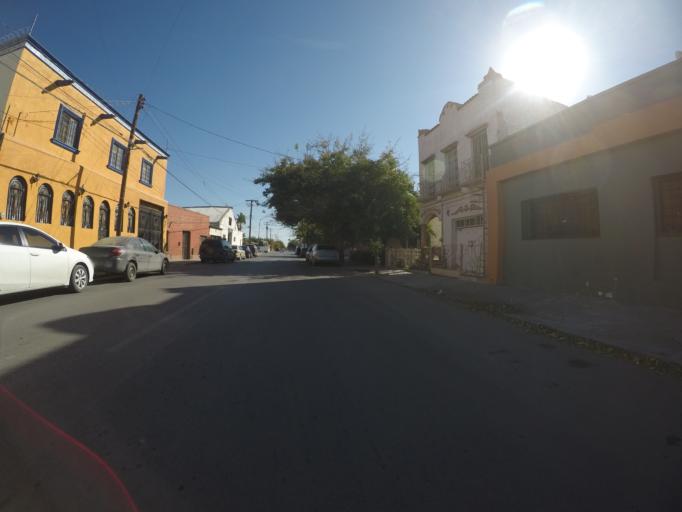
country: MX
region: Chihuahua
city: Ciudad Juarez
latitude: 31.7376
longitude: -106.4738
